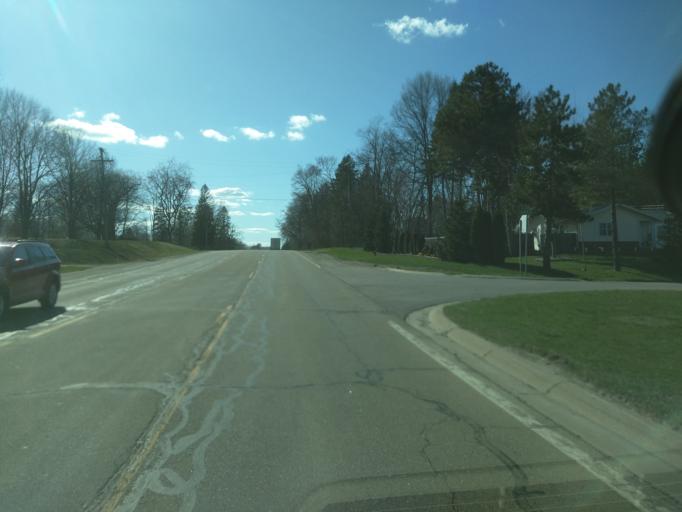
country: US
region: Michigan
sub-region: Eaton County
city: Waverly
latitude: 42.7823
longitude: -84.6560
